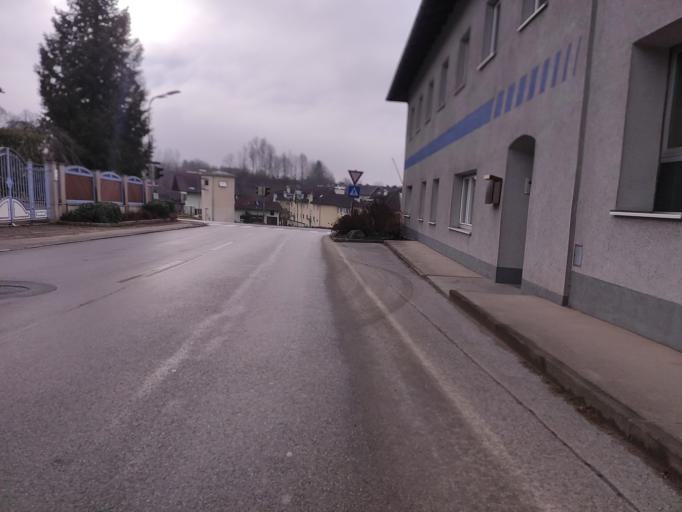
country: AT
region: Salzburg
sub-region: Politischer Bezirk Salzburg-Umgebung
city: Neumarkt am Wallersee
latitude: 47.9497
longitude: 13.2227
